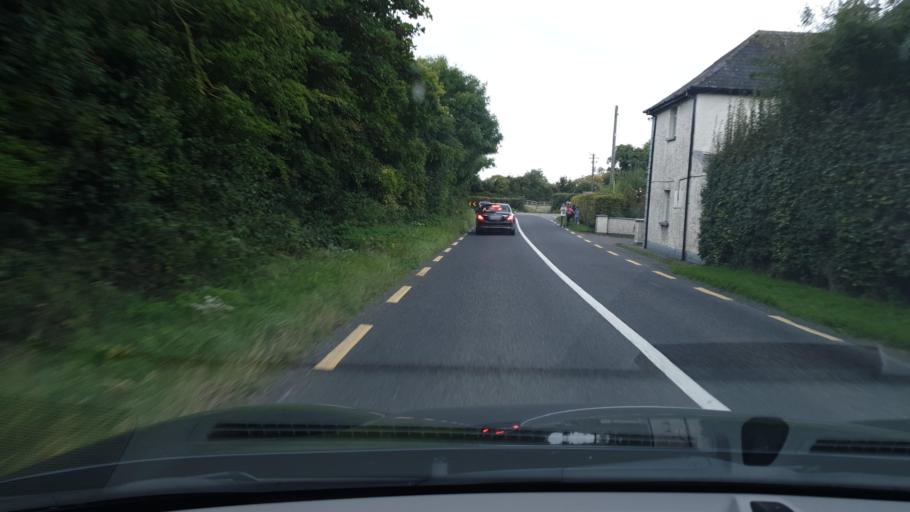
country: IE
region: Leinster
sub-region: An Mhi
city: Dunshaughlin
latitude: 53.5206
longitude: -6.5284
